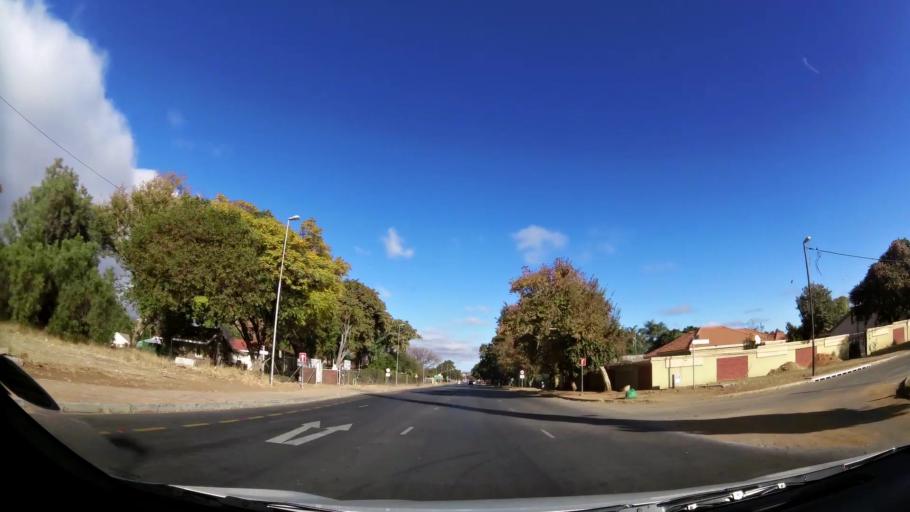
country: ZA
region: Limpopo
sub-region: Capricorn District Municipality
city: Polokwane
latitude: -23.9185
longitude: 29.4638
